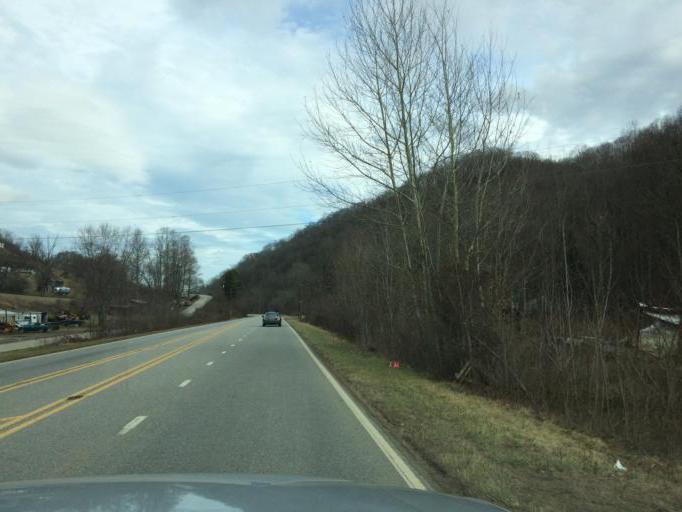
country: US
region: North Carolina
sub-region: Haywood County
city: Canton
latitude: 35.5366
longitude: -82.7938
